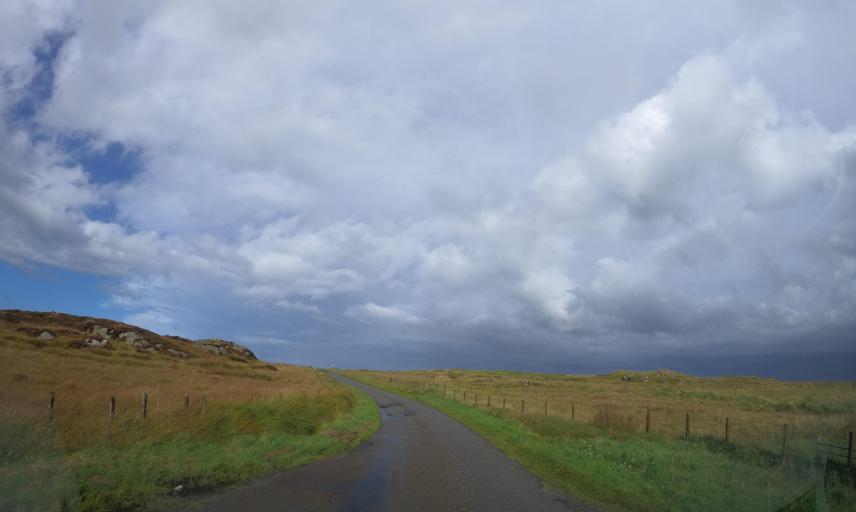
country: GB
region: Scotland
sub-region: Eilean Siar
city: Barra
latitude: 56.5216
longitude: -6.8421
